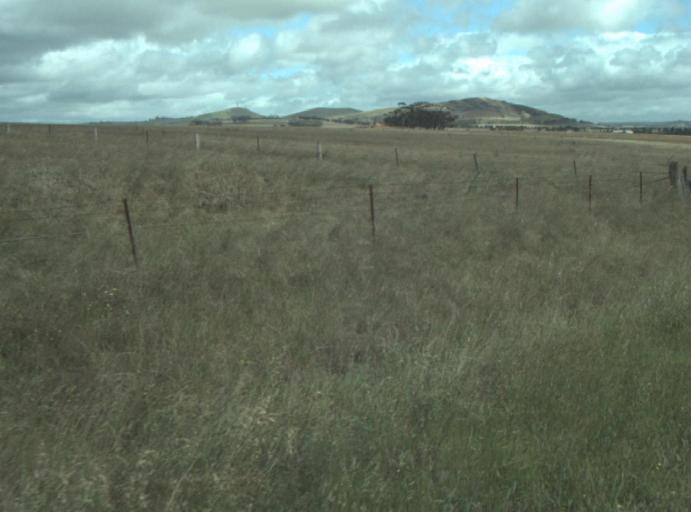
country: AU
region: Victoria
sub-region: Greater Geelong
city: Lara
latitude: -37.9354
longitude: 144.3108
